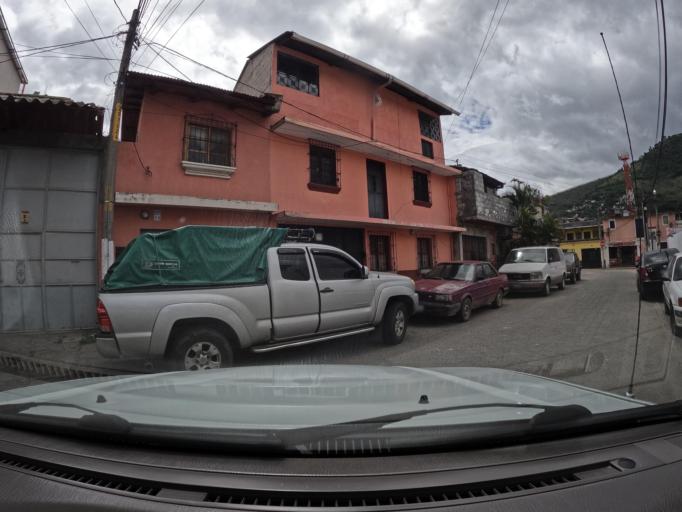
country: GT
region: Sacatepequez
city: Jocotenango
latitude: 14.5773
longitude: -90.7391
